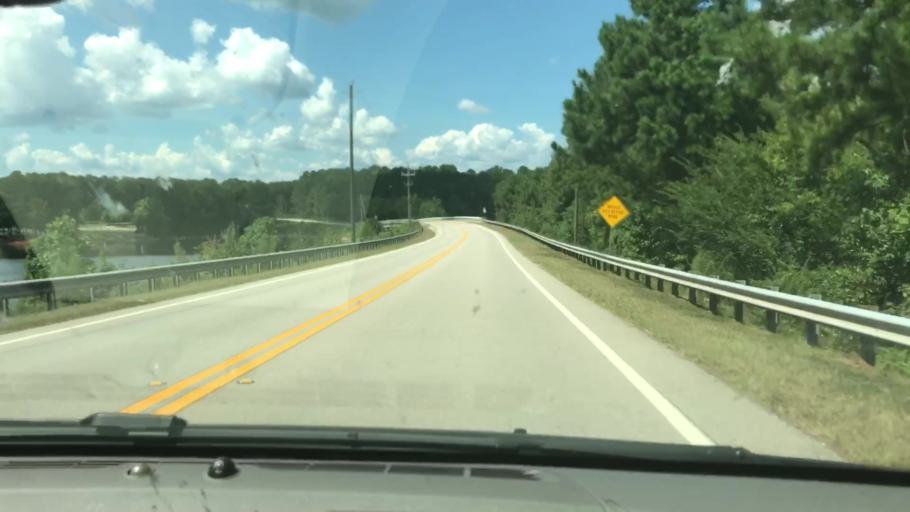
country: US
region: Georgia
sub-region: Troup County
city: La Grange
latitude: 33.0947
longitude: -85.0595
